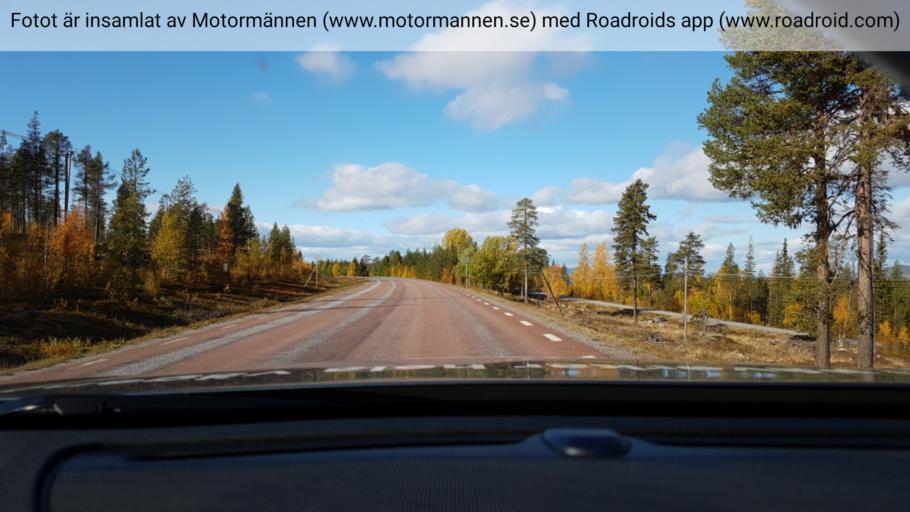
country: SE
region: Norrbotten
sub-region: Arjeplogs Kommun
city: Arjeplog
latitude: 66.0600
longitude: 17.9624
